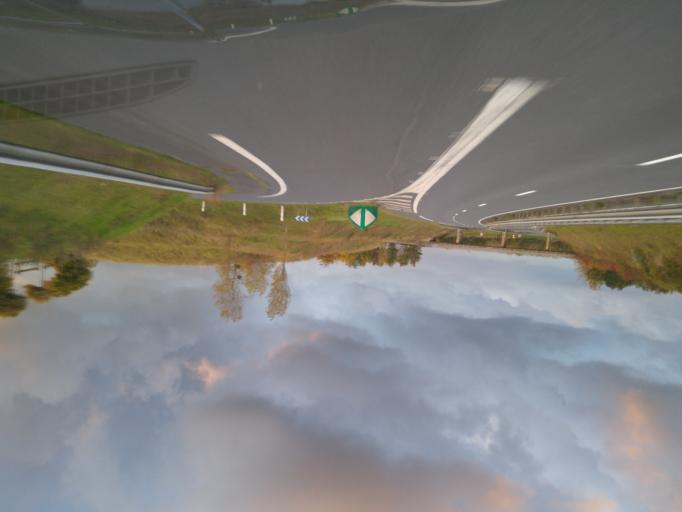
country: FR
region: Lower Normandy
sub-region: Departement du Calvados
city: Grandcamp-Maisy
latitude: 49.3385
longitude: -1.0098
